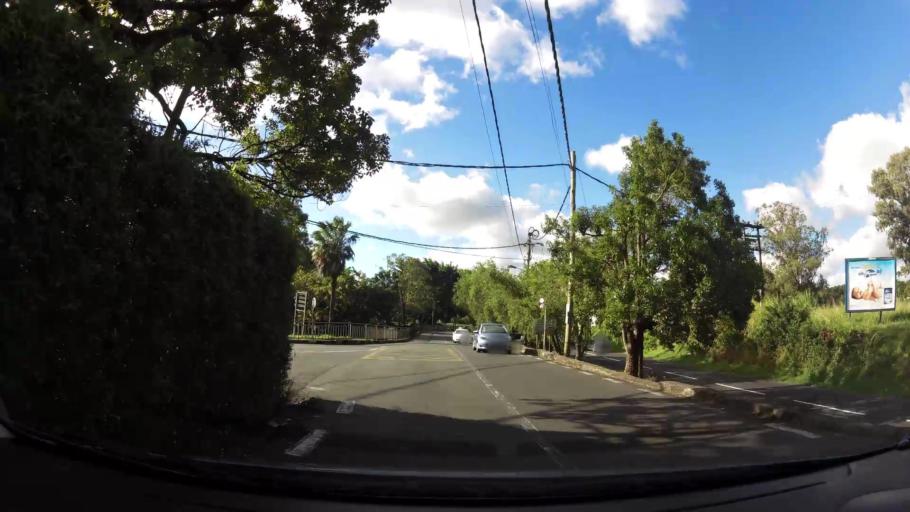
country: MU
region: Plaines Wilhems
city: Vacoas
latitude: -20.2847
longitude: 57.4973
